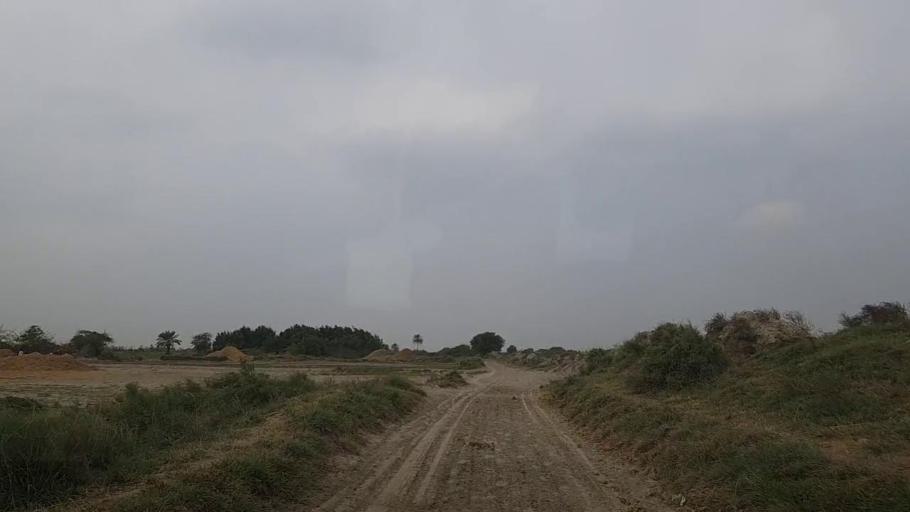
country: PK
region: Sindh
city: Mirpur Sakro
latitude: 24.5927
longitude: 67.6996
